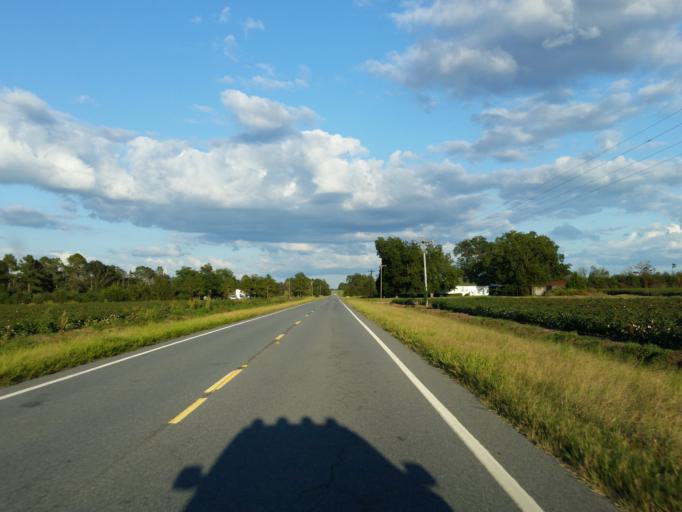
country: US
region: Georgia
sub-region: Dooly County
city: Vienna
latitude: 32.0863
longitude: -83.7458
